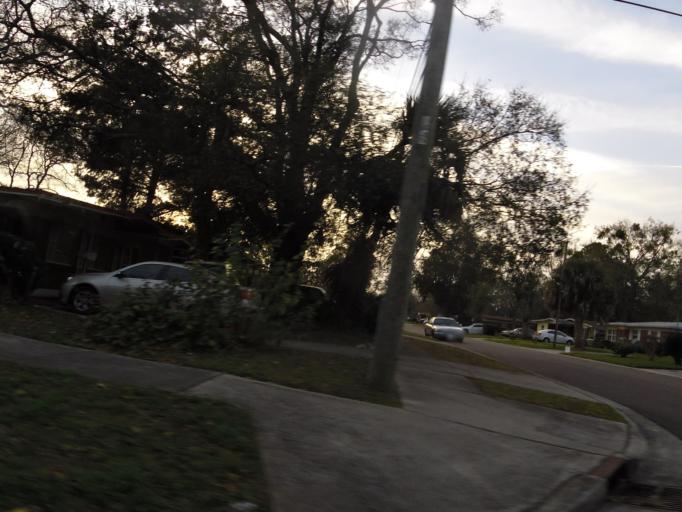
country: US
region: Florida
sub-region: Duval County
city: Jacksonville
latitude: 30.3610
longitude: -81.7051
